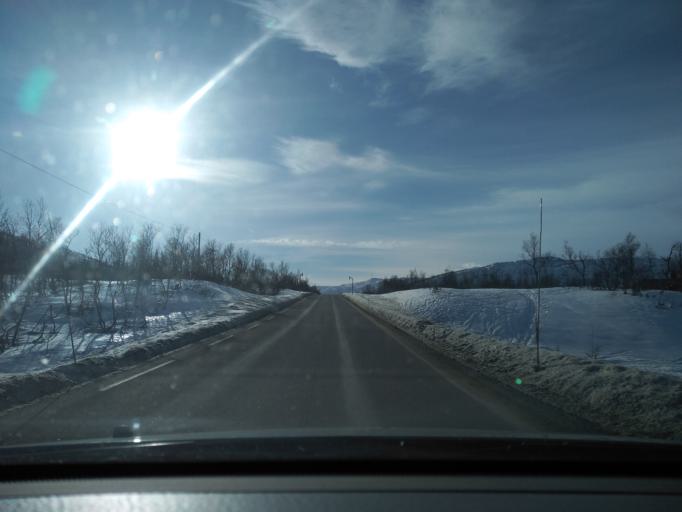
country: NO
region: Aust-Agder
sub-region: Bykle
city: Hovden
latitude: 59.6479
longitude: 7.4687
